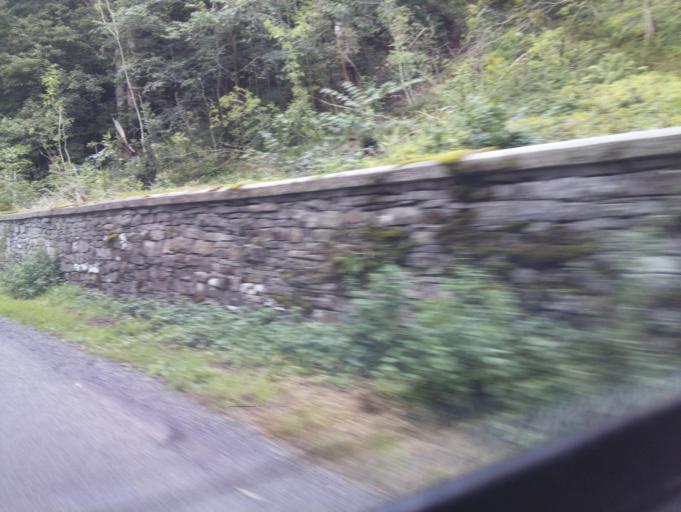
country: GB
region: England
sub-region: North Yorkshire
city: Leyburn
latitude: 54.3997
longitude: -1.8240
